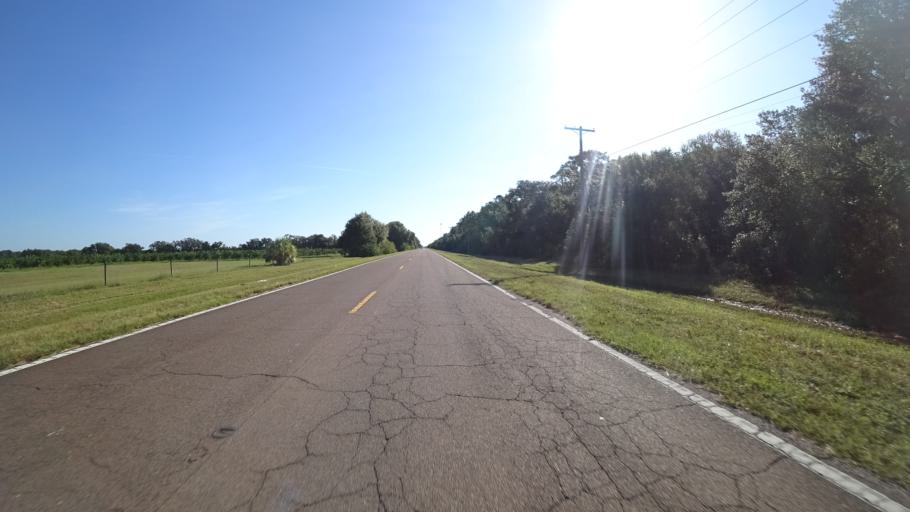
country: US
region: Florida
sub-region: Hillsborough County
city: Ruskin
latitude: 27.6537
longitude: -82.5052
